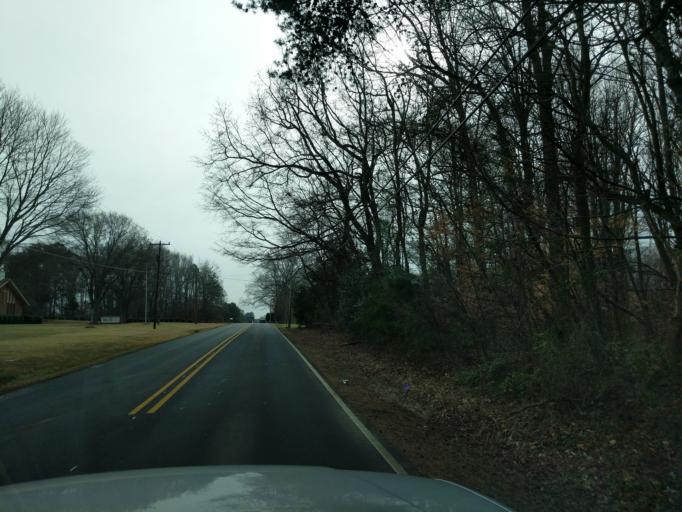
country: US
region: North Carolina
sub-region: Mecklenburg County
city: Charlotte
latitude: 35.3161
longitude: -80.8849
